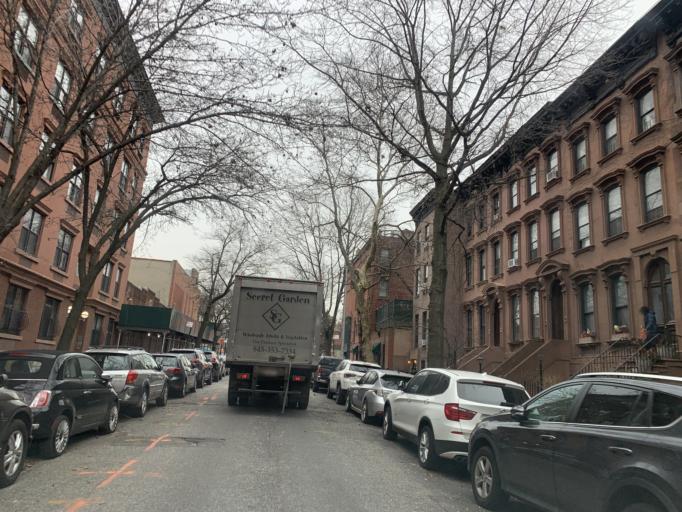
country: US
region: New York
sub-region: Kings County
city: Brooklyn
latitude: 40.6781
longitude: -73.9742
